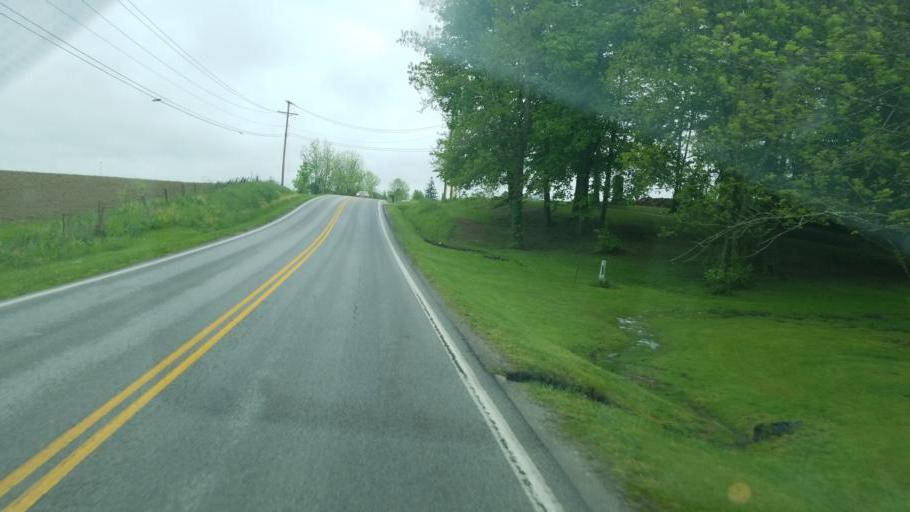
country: US
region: Ohio
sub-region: Highland County
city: Hillsboro
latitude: 39.2219
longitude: -83.6208
